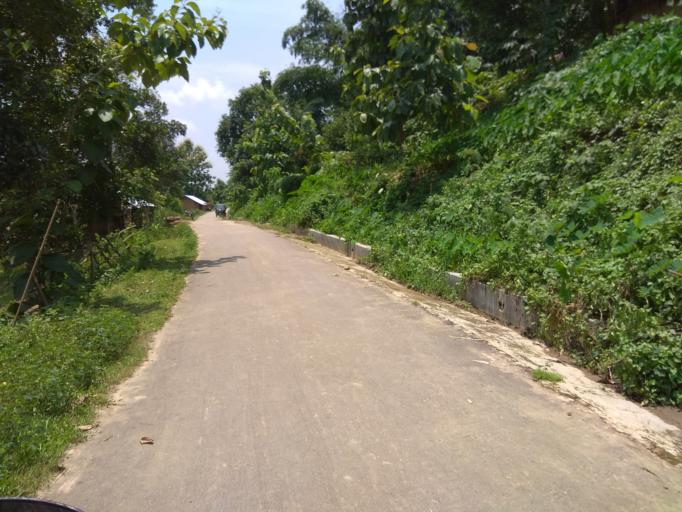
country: BD
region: Chittagong
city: Manikchari
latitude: 22.8971
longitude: 91.9239
